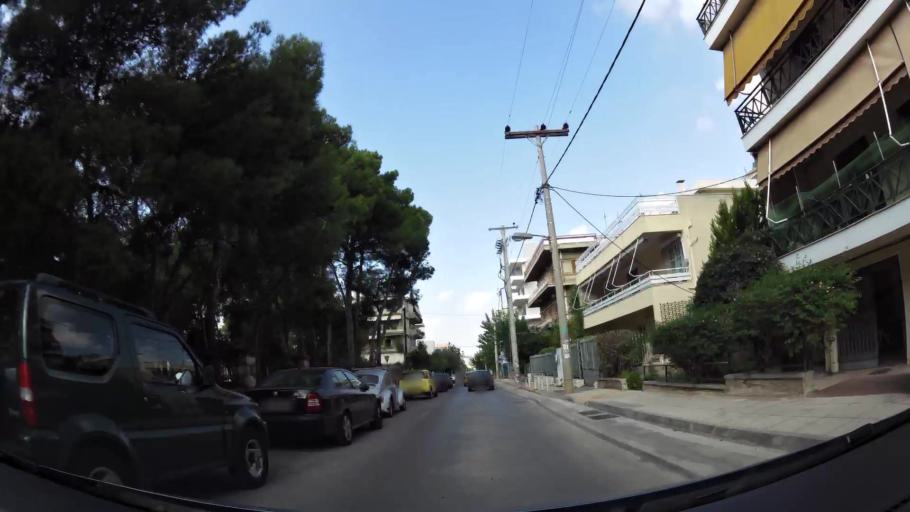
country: GR
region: Attica
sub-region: Nomarchia Athinas
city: Cholargos
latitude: 37.9968
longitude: 23.7921
